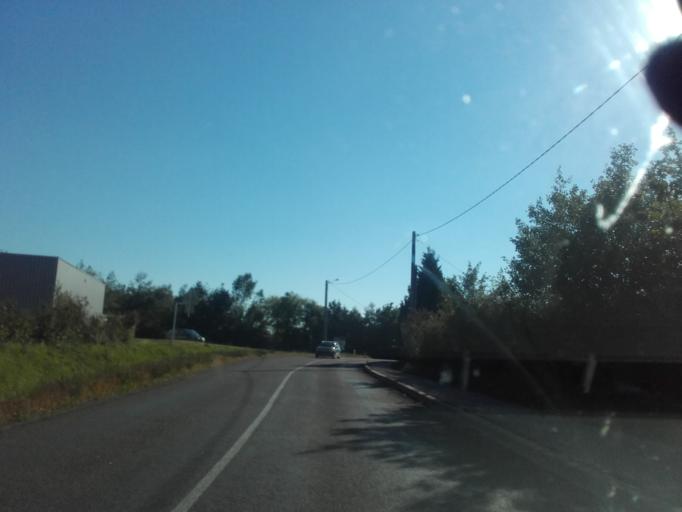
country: FR
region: Bourgogne
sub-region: Departement de Saone-et-Loire
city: Chagny
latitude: 46.9096
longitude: 4.7645
